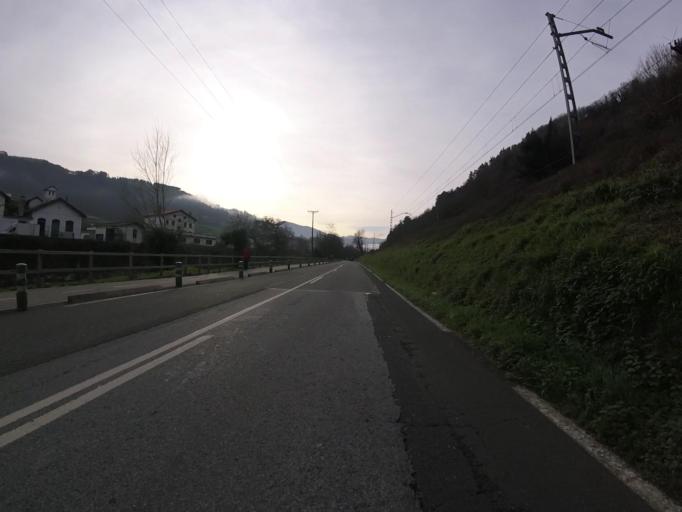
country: ES
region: Basque Country
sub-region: Provincia de Guipuzcoa
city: Anoeta
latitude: 43.1488
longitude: -2.0725
